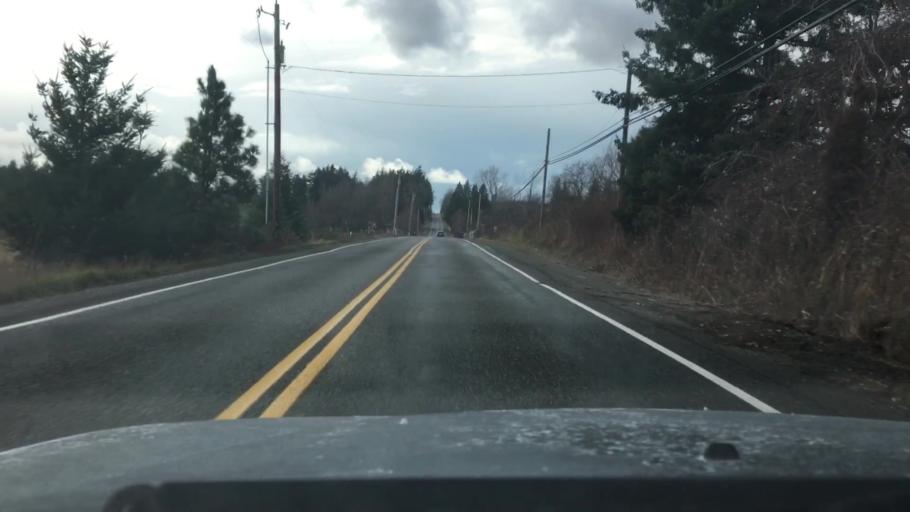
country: US
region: Washington
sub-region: Whatcom County
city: Ferndale
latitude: 48.8484
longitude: -122.6638
